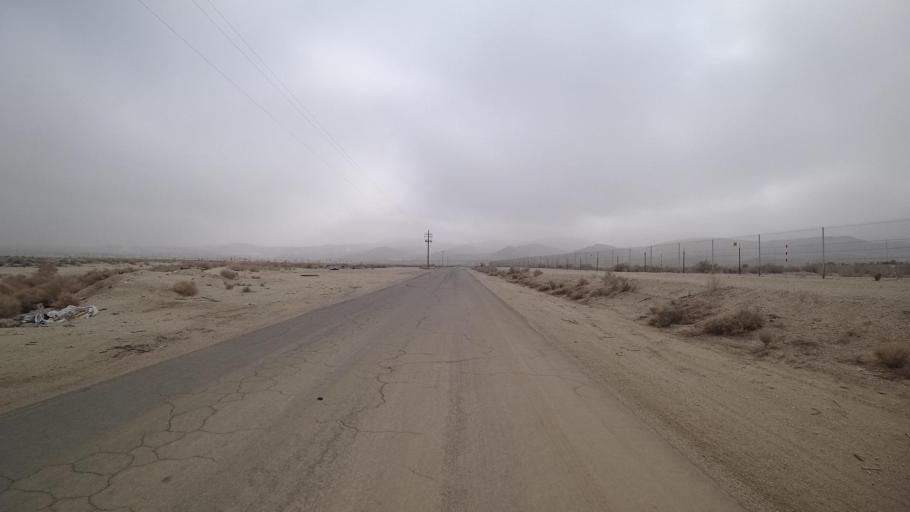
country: US
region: California
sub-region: Kern County
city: Maricopa
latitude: 35.0484
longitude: -119.3920
